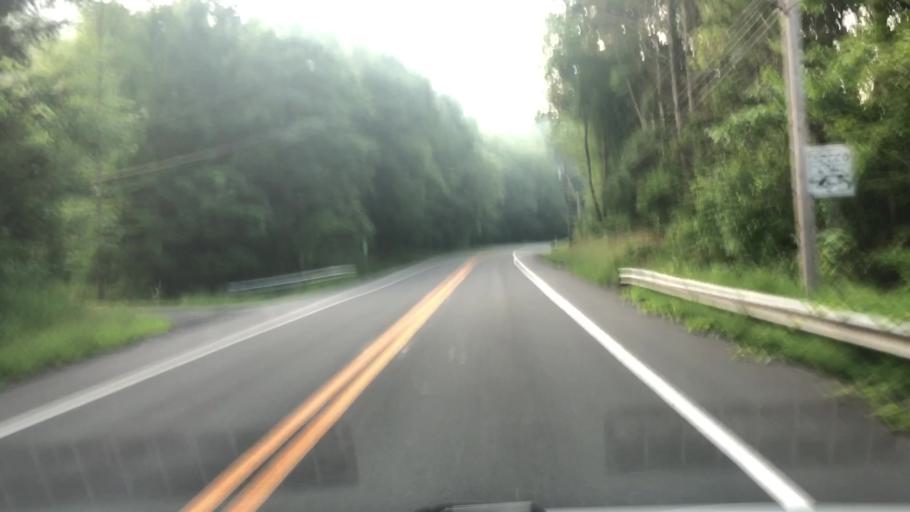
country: US
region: Massachusetts
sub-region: Franklin County
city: Ashfield
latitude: 42.5525
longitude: -72.8037
